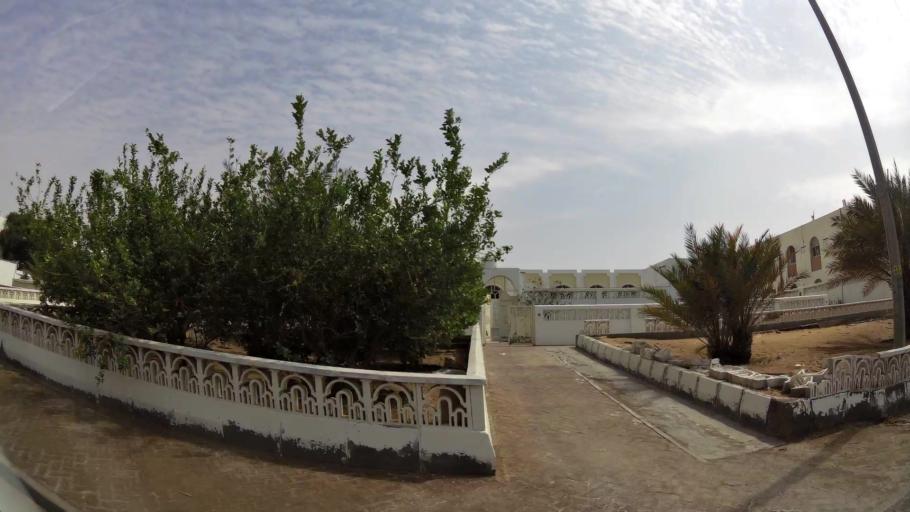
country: AE
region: Abu Dhabi
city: Abu Dhabi
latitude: 24.5224
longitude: 54.6628
